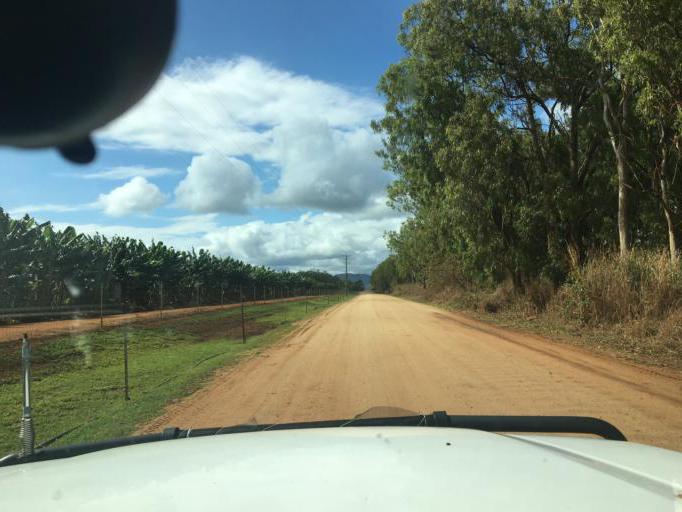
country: AU
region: Queensland
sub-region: Tablelands
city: Mareeba
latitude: -17.0956
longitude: 145.4122
